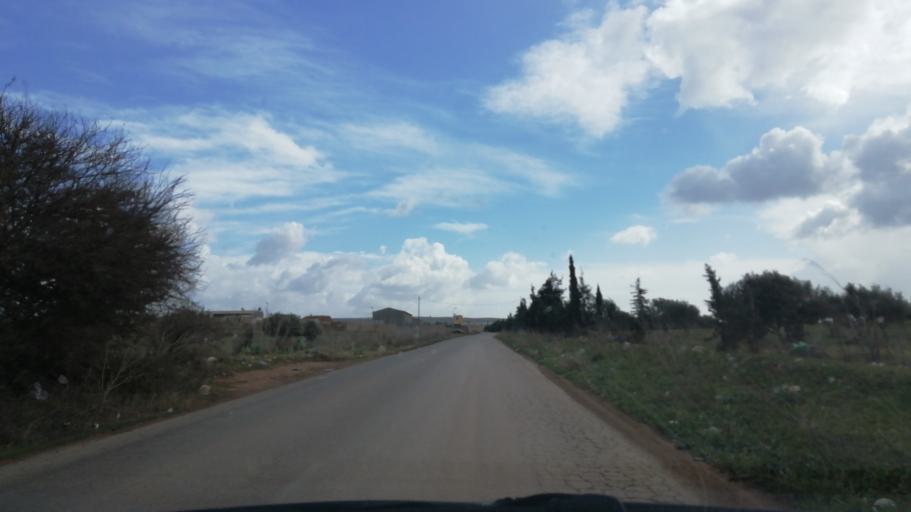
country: DZ
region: Oran
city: Sidi ech Chahmi
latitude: 35.6347
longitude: -0.5346
